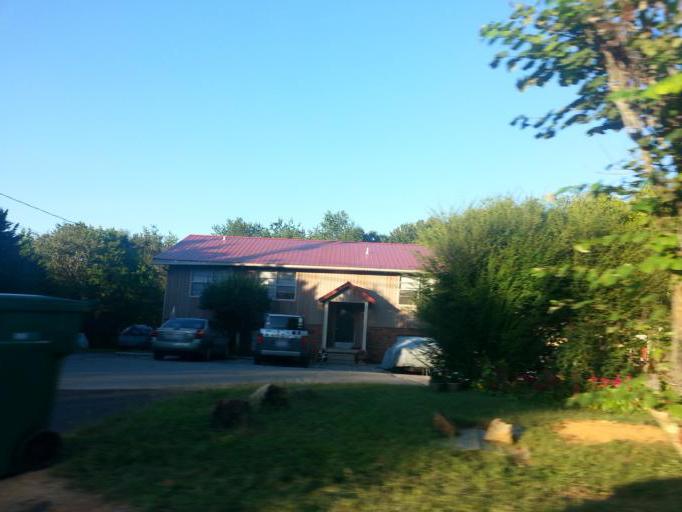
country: US
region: Tennessee
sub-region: Blount County
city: Alcoa
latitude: 35.8354
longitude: -83.9791
